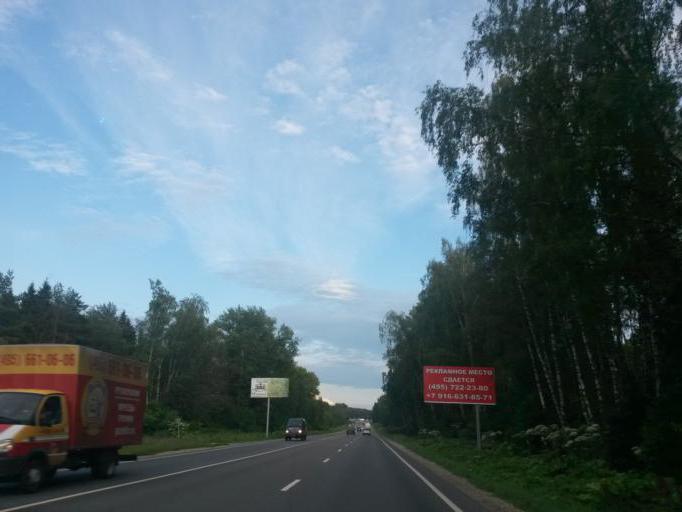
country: RU
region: Moskovskaya
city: Barybino
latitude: 55.2409
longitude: 37.8556
